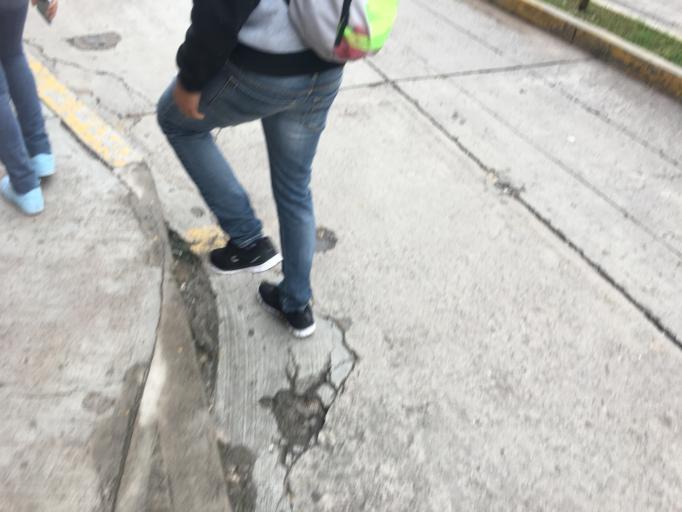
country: MX
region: Oaxaca
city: Ciudad de Huajuapam de Leon
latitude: 17.8071
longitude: -97.7750
